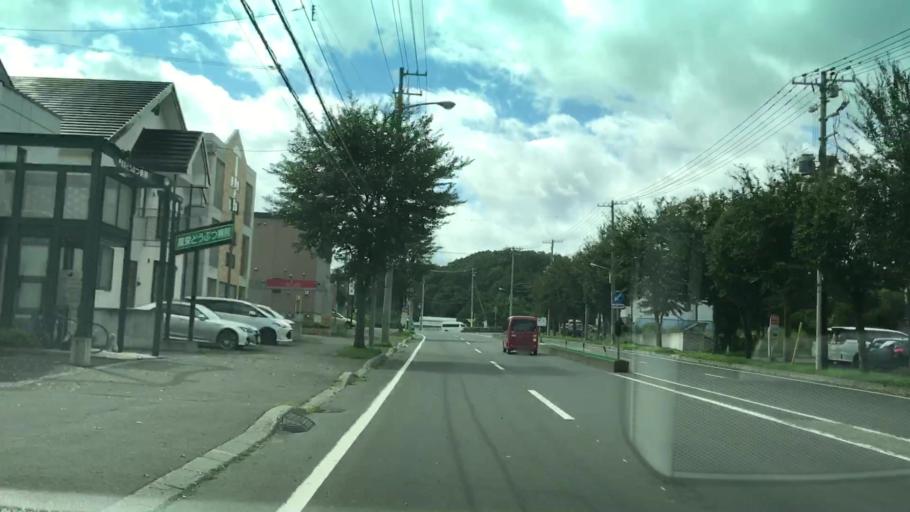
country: JP
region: Hokkaido
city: Sapporo
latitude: 42.9839
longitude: 141.4383
